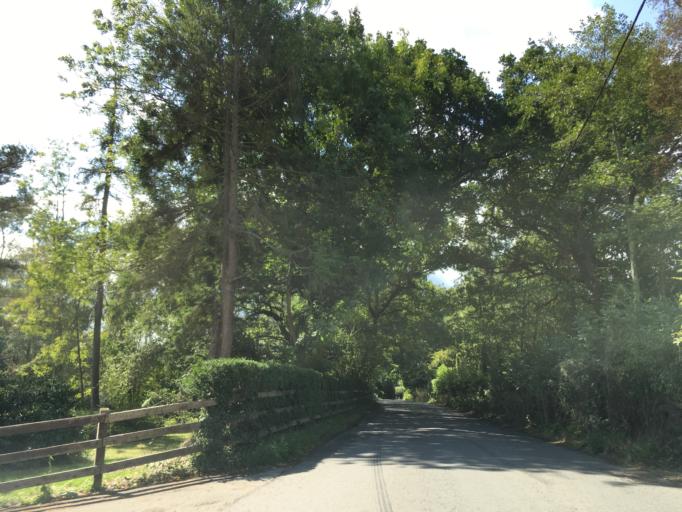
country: GB
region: England
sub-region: Hampshire
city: Colden Common
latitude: 50.9904
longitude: -1.3002
